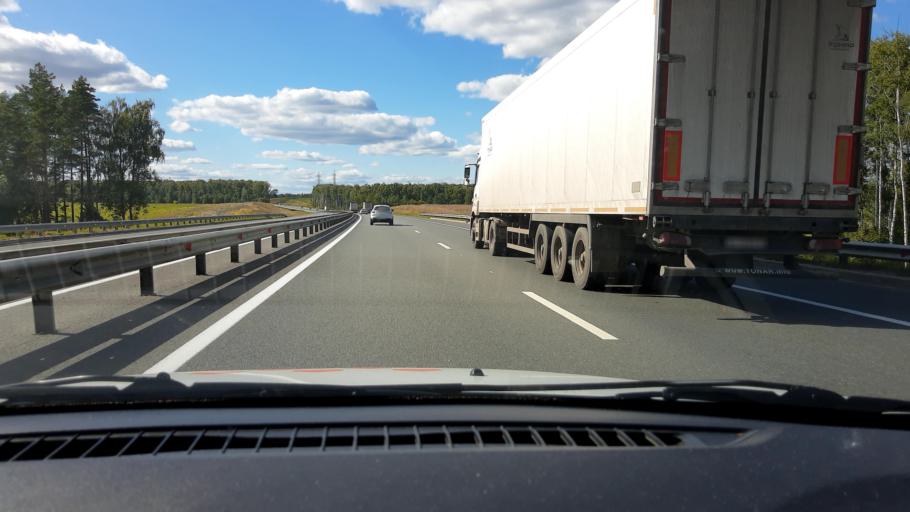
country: RU
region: Nizjnij Novgorod
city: Kstovo
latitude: 56.0966
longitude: 44.0687
